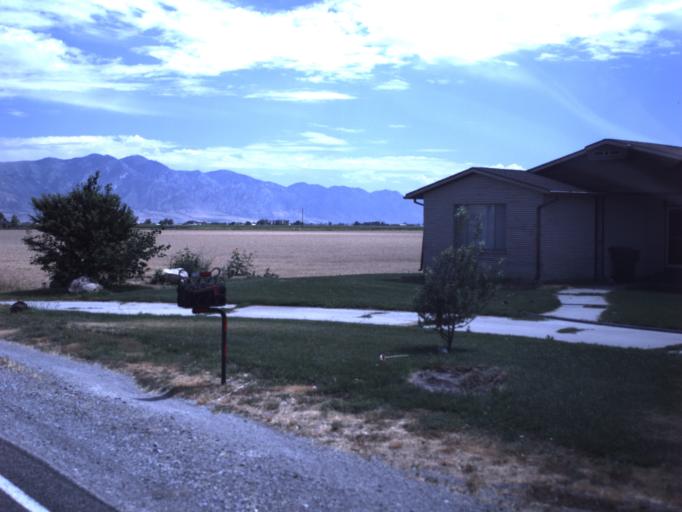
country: US
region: Utah
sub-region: Box Elder County
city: Tremonton
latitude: 41.7099
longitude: -112.2432
